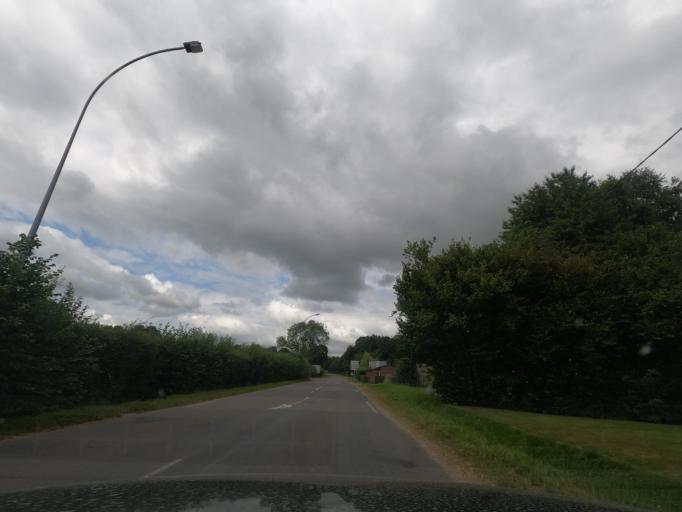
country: FR
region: Lower Normandy
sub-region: Departement de l'Orne
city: Briouze
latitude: 48.7034
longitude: -0.3648
